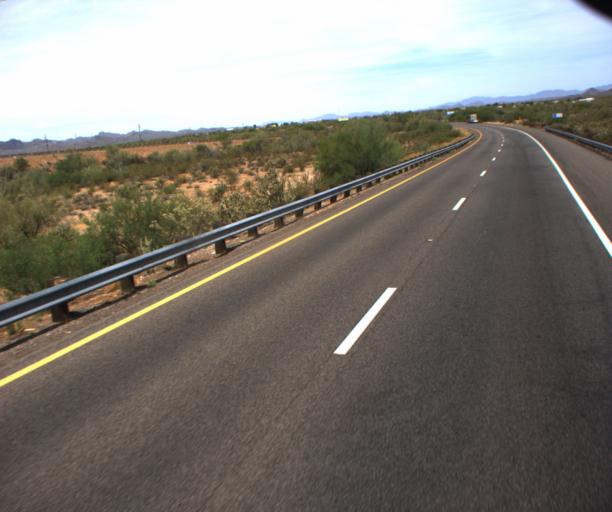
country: US
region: Arizona
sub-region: Maricopa County
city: Wickenburg
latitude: 33.8451
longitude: -112.6119
